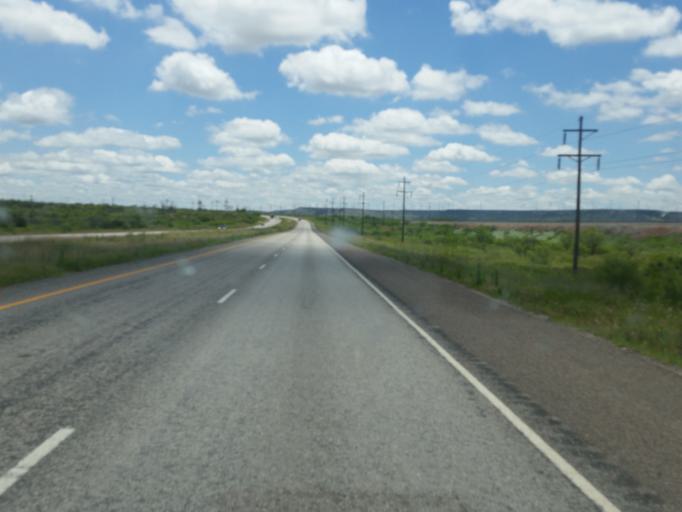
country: US
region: Texas
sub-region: Garza County
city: Post
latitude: 33.0062
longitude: -101.1671
